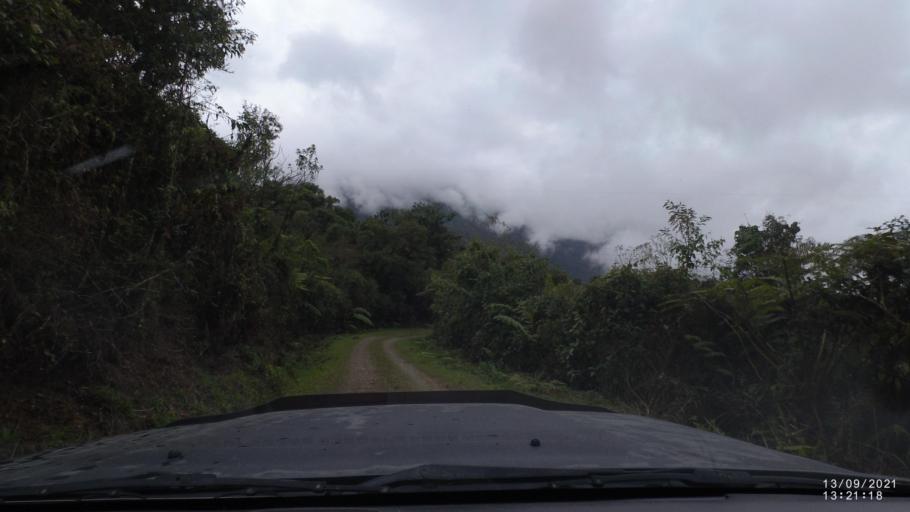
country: BO
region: Cochabamba
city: Colomi
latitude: -17.2081
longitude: -65.8616
